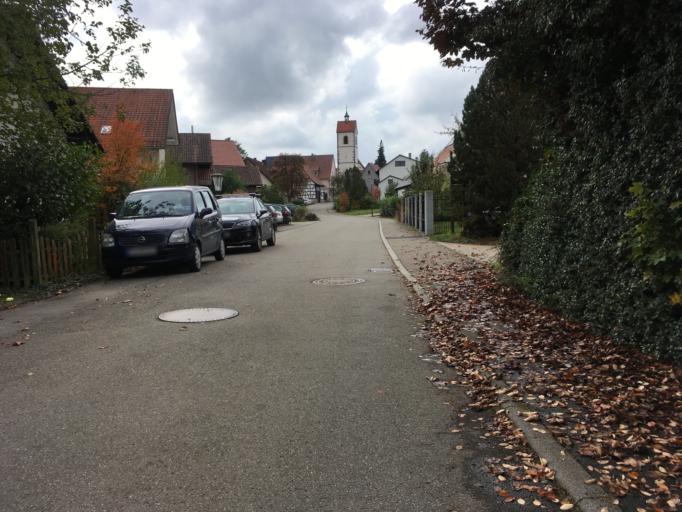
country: DE
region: Baden-Wuerttemberg
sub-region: Tuebingen Region
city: Gomaringen
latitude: 48.4853
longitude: 9.1150
